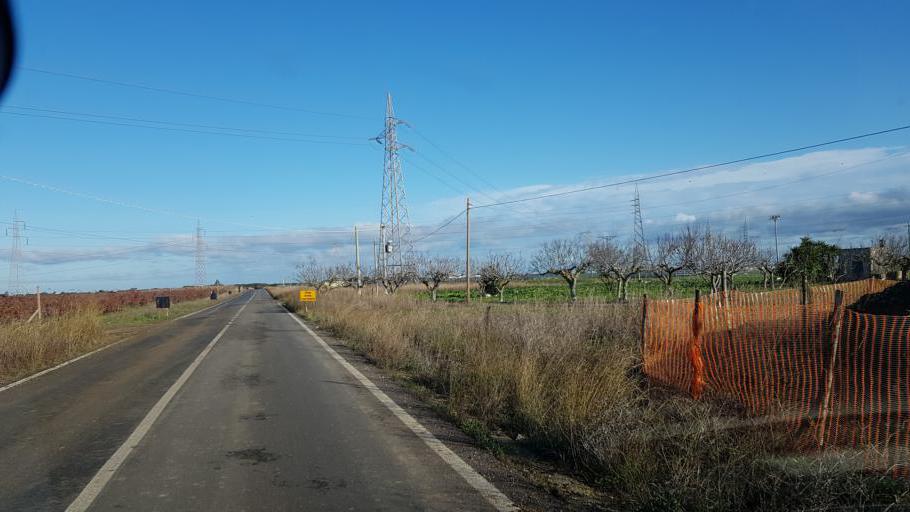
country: IT
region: Apulia
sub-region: Provincia di Brindisi
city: Tuturano
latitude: 40.5530
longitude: 17.9469
